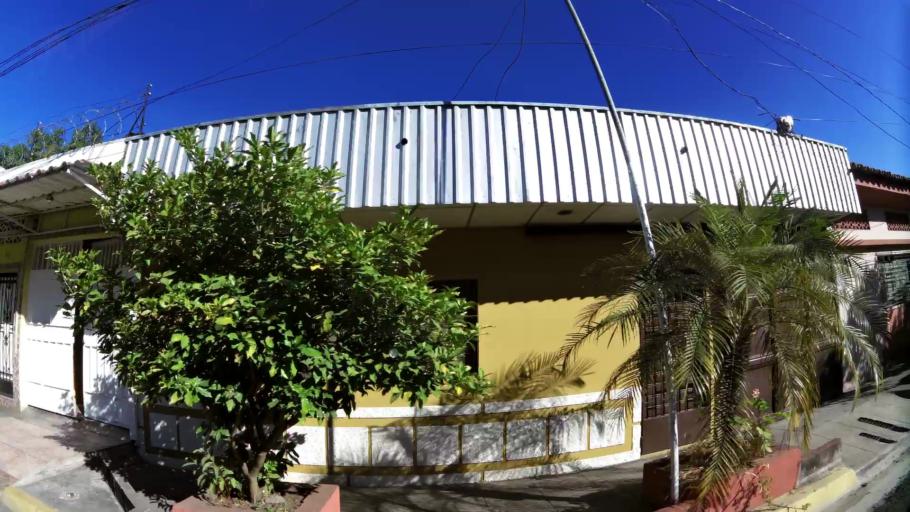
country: SV
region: San Miguel
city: San Miguel
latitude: 13.4794
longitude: -88.1726
